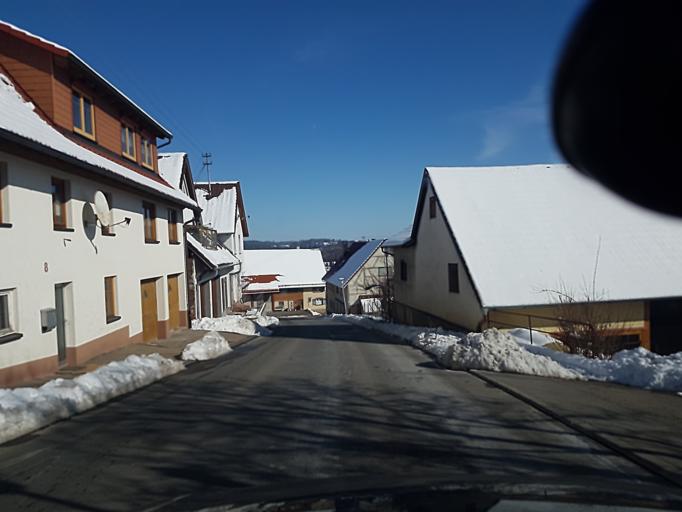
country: DE
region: Baden-Wuerttemberg
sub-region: Freiburg Region
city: Niedereschach
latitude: 48.1651
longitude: 8.5238
